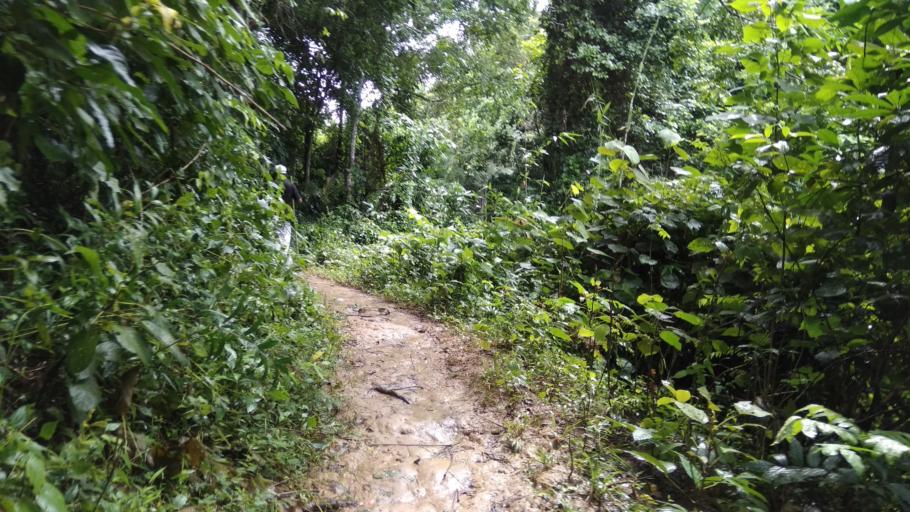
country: IN
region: Tripura
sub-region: Dhalai
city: Kamalpur
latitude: 24.1731
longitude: 91.8871
